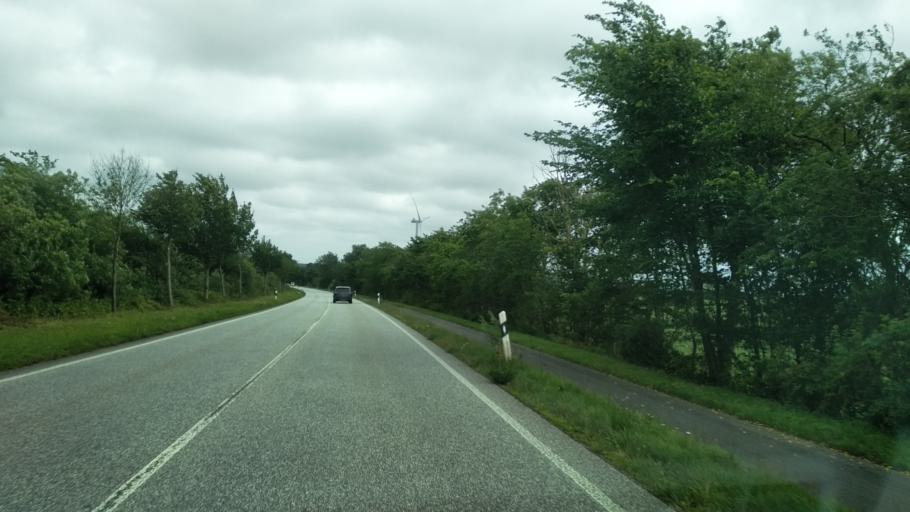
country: DE
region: Schleswig-Holstein
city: Sieverstedt
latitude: 54.6544
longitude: 9.4428
